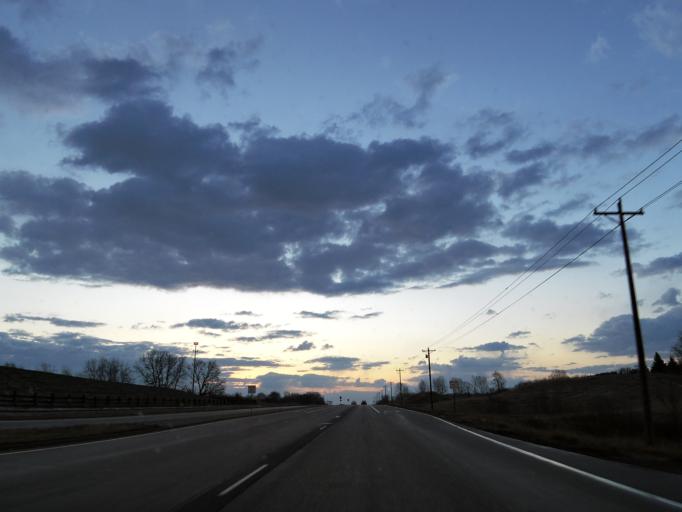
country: US
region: Minnesota
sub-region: Dakota County
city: Lakeville
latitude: 44.6814
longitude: -93.3281
